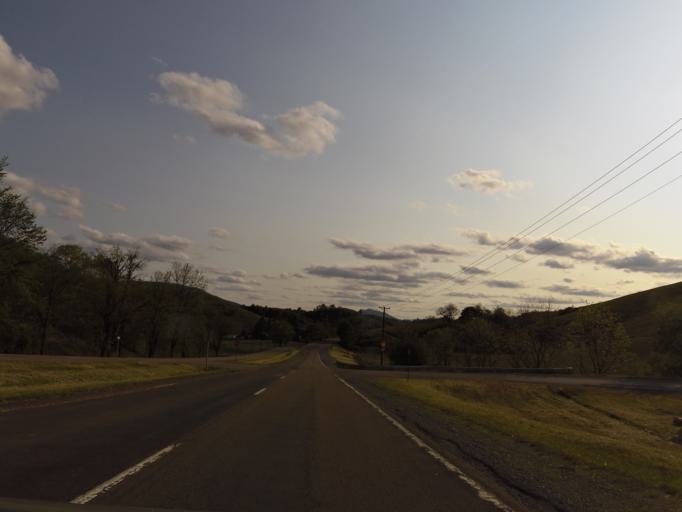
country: US
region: Virginia
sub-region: Tazewell County
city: Springville
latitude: 37.1615
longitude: -81.4636
